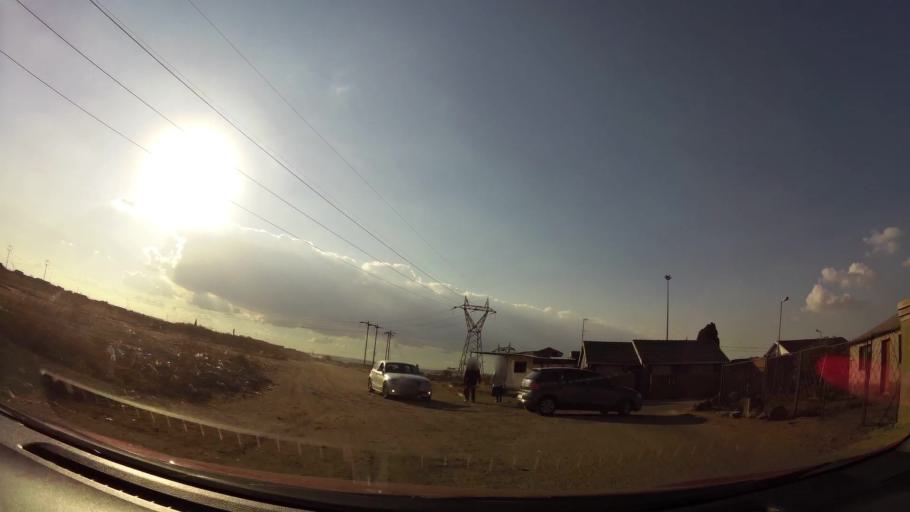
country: ZA
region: Gauteng
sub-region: City of Johannesburg Metropolitan Municipality
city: Soweto
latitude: -26.2320
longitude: 27.8586
